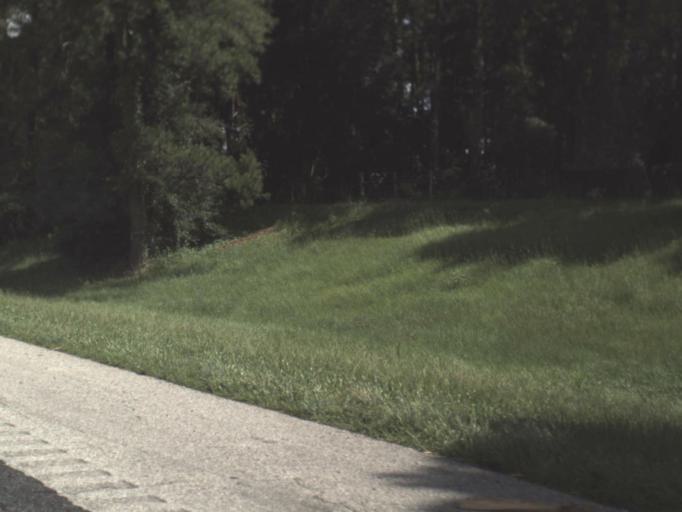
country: US
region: Florida
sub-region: Alachua County
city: High Springs
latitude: 29.8278
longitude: -82.5216
